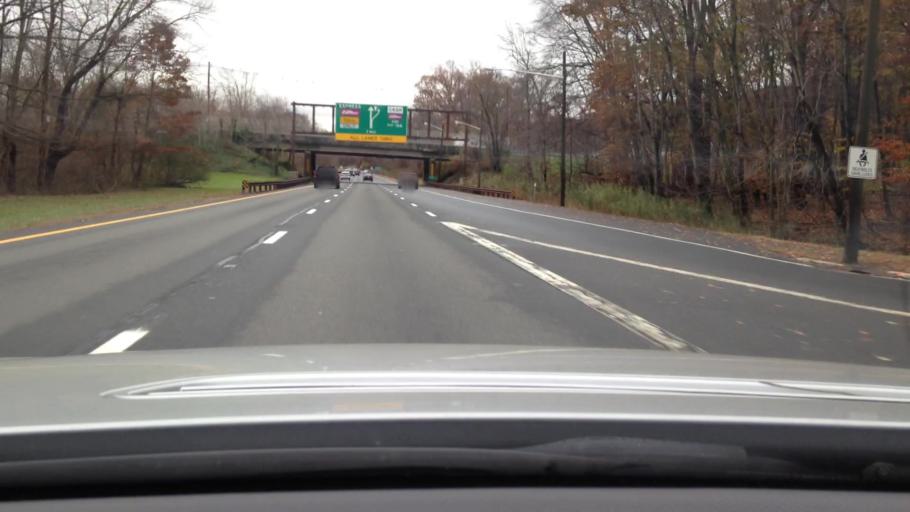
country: US
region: New Jersey
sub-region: Bergen County
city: Woodcliff Lake
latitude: 41.0002
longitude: -74.0715
